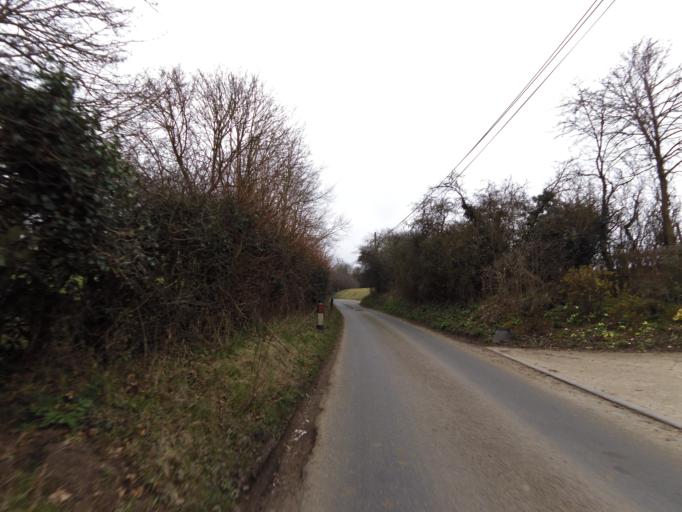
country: GB
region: England
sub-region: Suffolk
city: Framlingham
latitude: 52.2222
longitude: 1.3265
